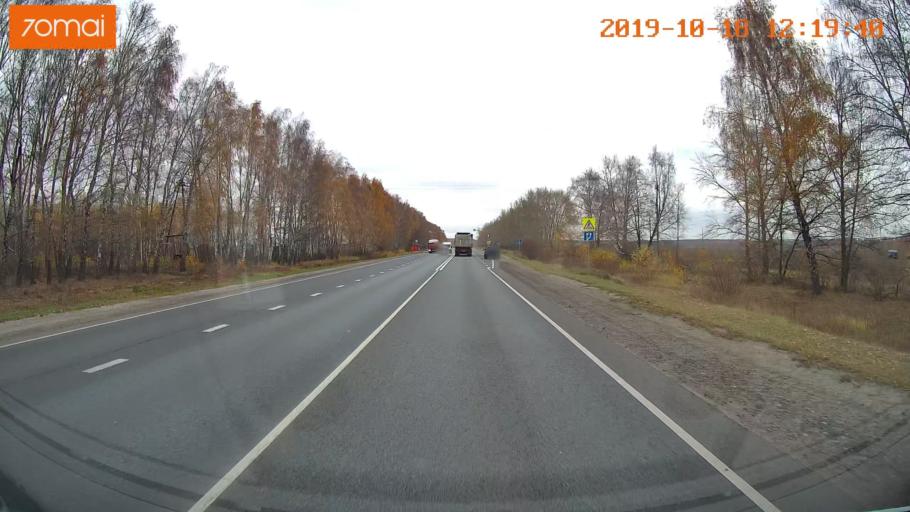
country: RU
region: Rjazan
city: Zakharovo
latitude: 54.4860
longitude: 39.4710
